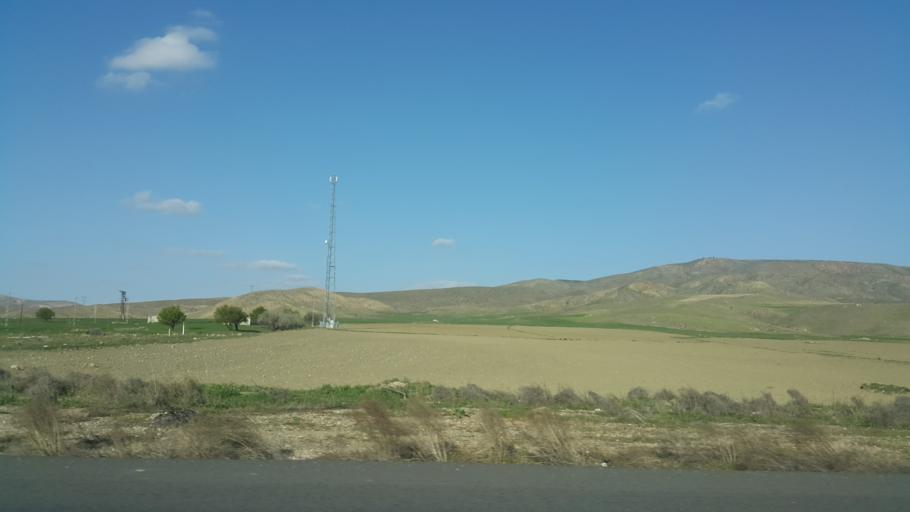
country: TR
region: Ankara
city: Sereflikochisar
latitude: 38.8367
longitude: 33.5914
